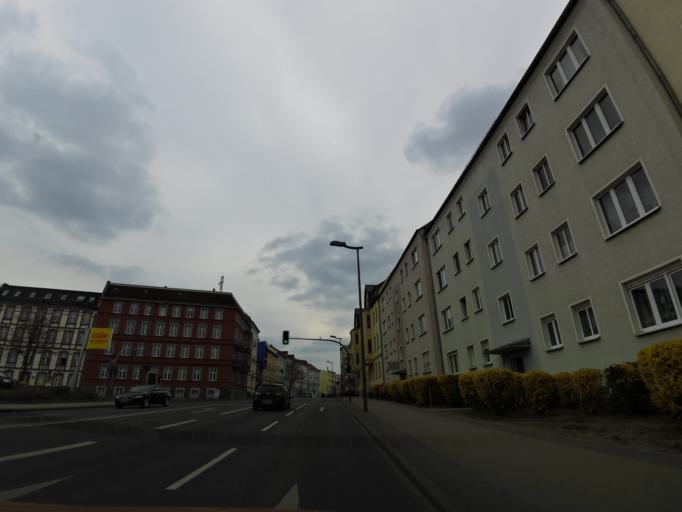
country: DE
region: Brandenburg
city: Frankfurt (Oder)
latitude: 52.3385
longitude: 14.5395
